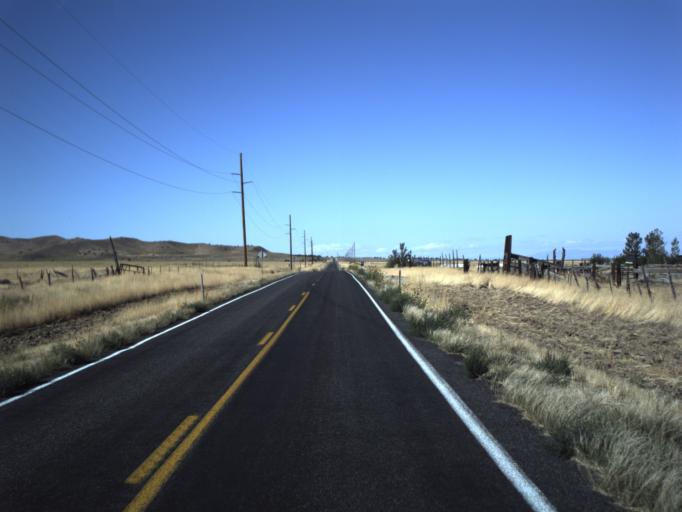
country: US
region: Utah
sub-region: Millard County
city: Delta
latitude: 39.4697
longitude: -112.2728
